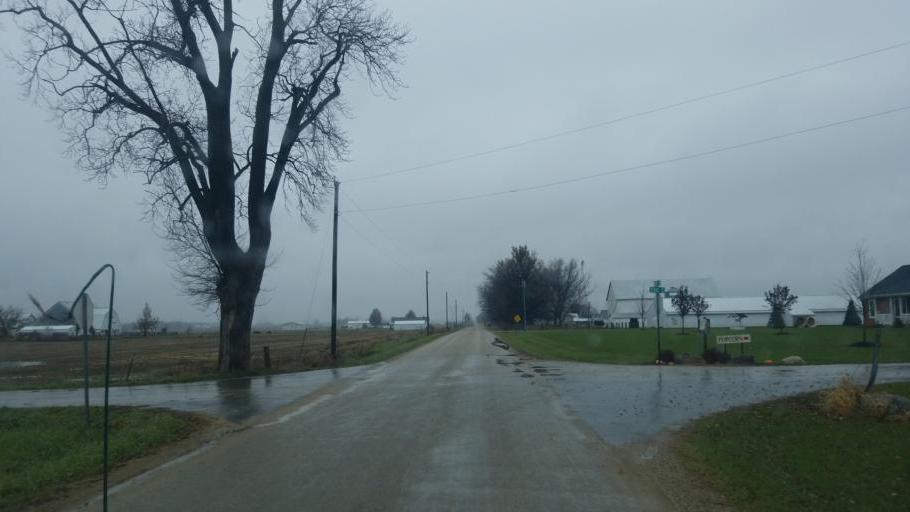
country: US
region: Indiana
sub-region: Adams County
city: Berne
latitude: 40.6655
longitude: -84.9173
